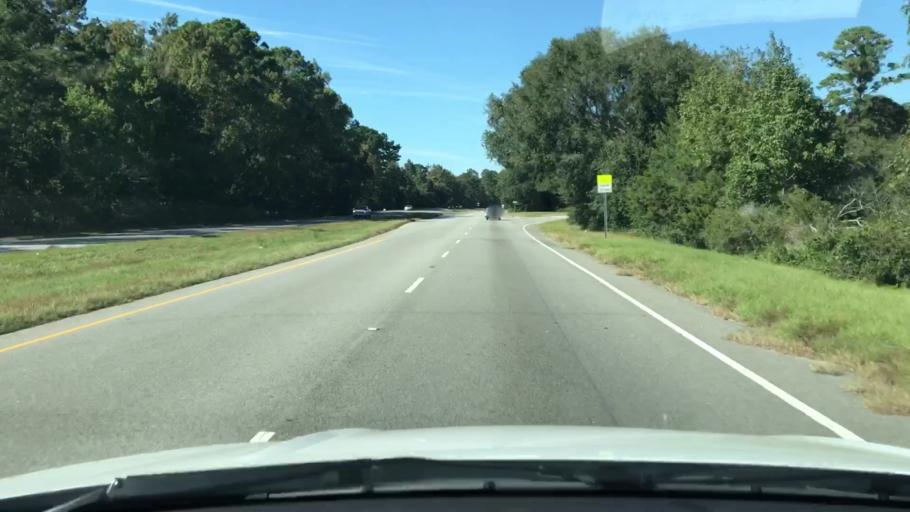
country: US
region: South Carolina
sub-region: Beaufort County
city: Laurel Bay
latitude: 32.5107
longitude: -80.7490
